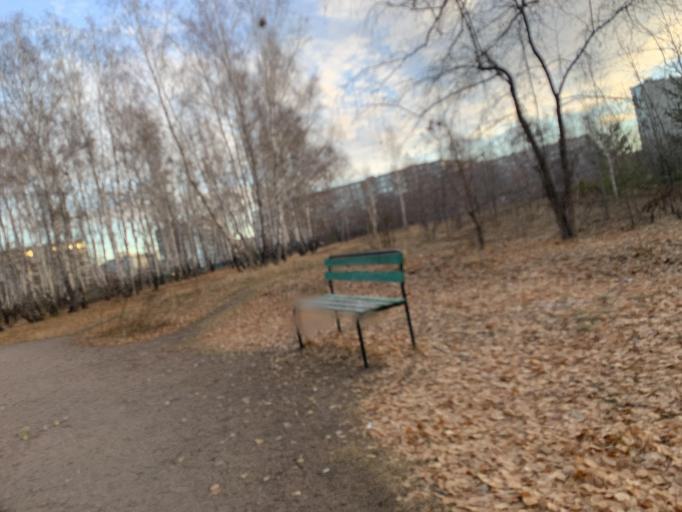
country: RU
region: Chelyabinsk
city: Roshchino
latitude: 55.2005
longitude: 61.3088
